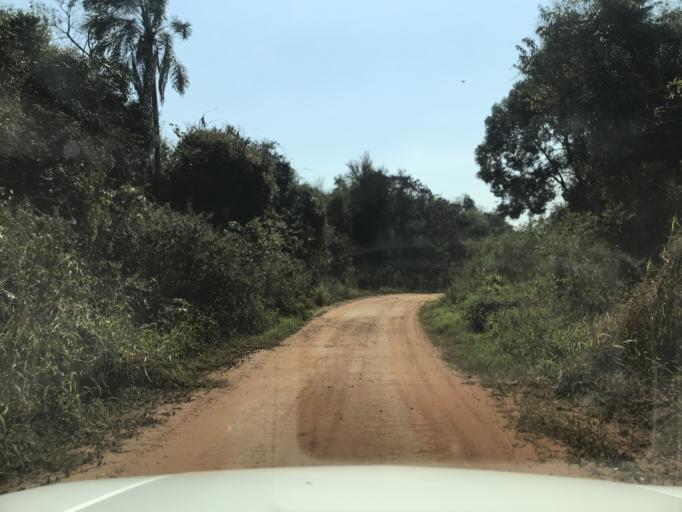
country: BR
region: Parana
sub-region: Palotina
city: Palotina
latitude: -24.2214
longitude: -53.7369
